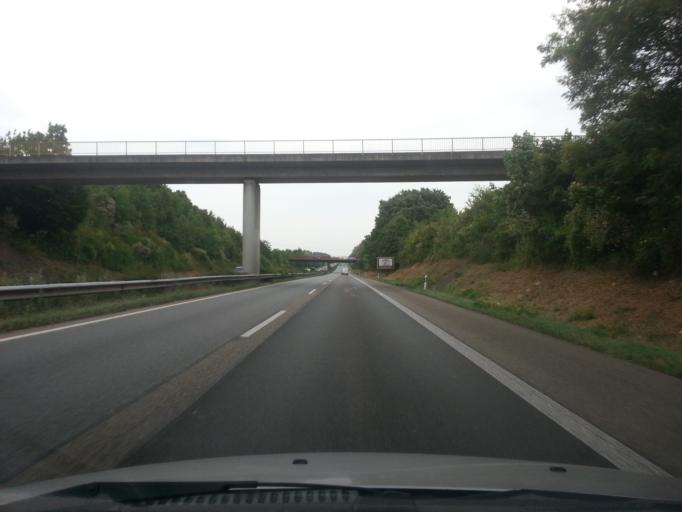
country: DE
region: Rheinland-Pfalz
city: Knoringen
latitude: 49.2400
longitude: 8.1487
